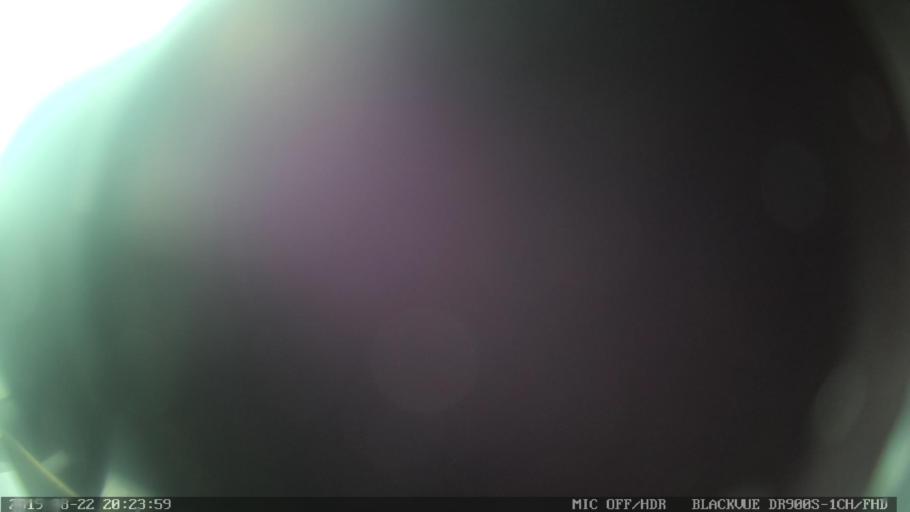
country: PT
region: Castelo Branco
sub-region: Castelo Branco
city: Castelo Branco
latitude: 39.8437
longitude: -7.5173
